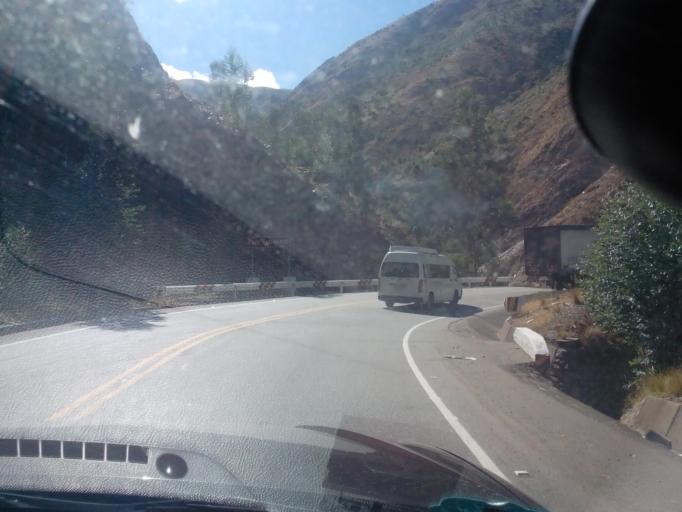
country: PE
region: Cusco
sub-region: Provincia de Quispicanchis
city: Urcos
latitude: -13.6866
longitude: -71.5944
